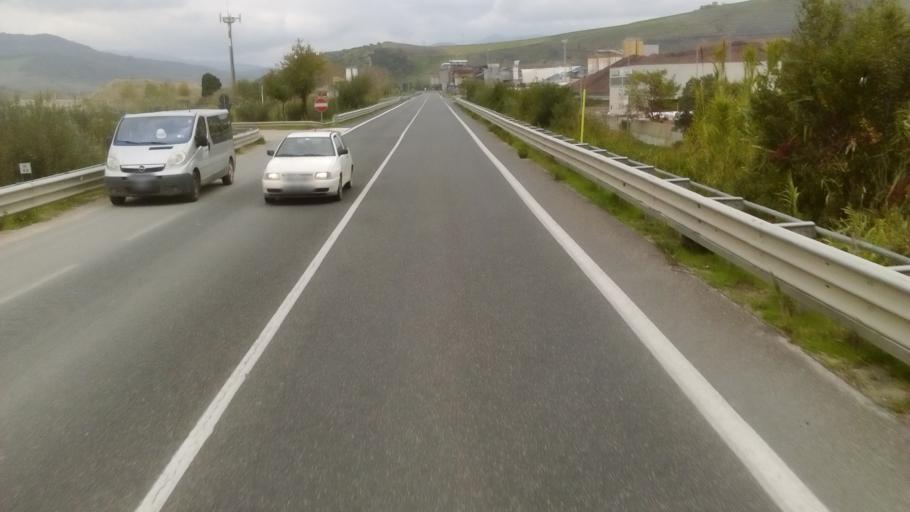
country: IT
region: Abruzzo
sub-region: Provincia di Chieti
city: Lentella
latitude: 41.9986
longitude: 14.7173
